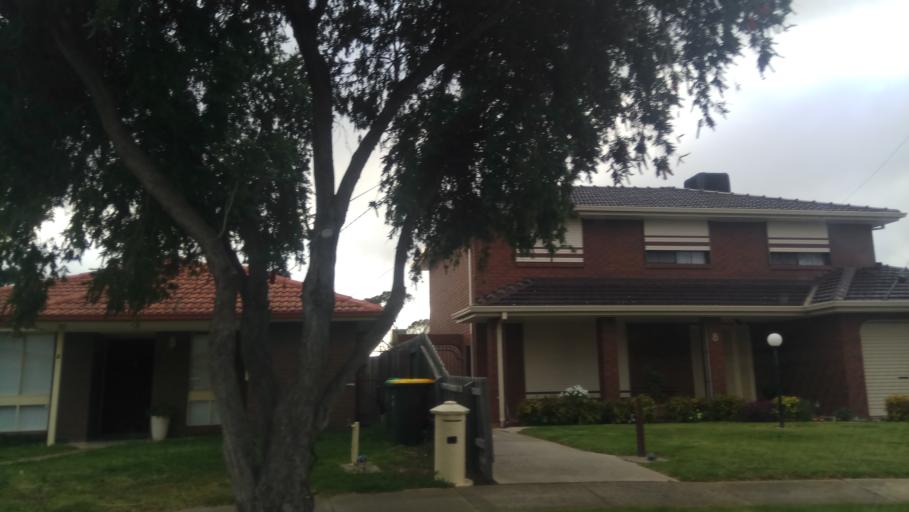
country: AU
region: Victoria
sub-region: Hobsons Bay
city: Altona Meadows
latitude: -37.8832
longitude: 144.7812
